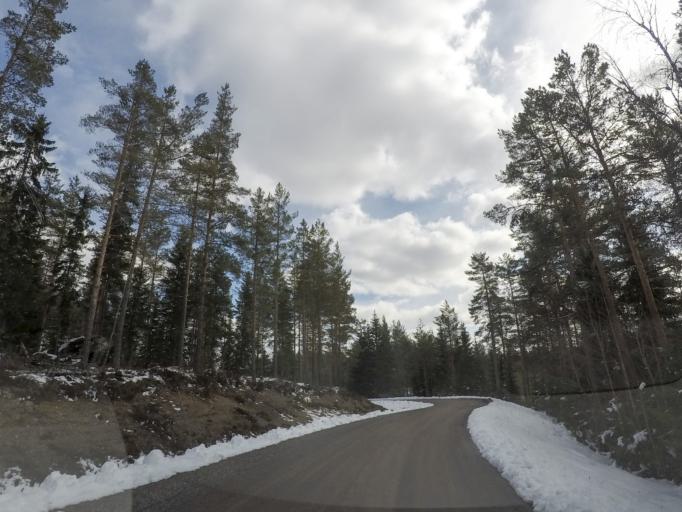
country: SE
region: OErebro
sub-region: Hallefors Kommun
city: Haellefors
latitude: 60.0157
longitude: 14.5879
